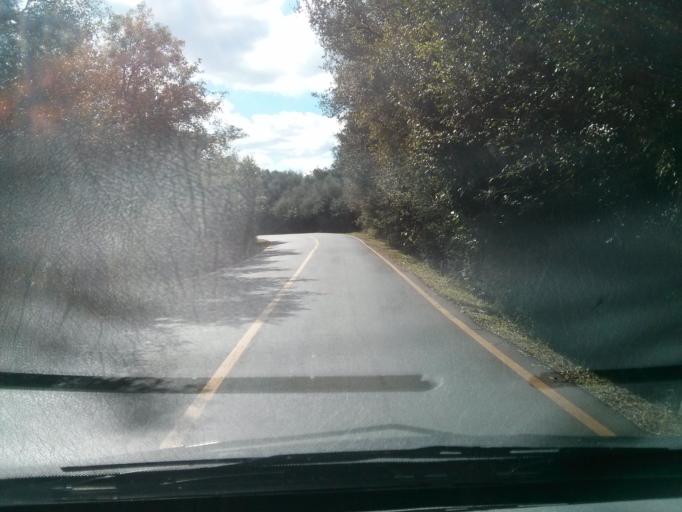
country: BR
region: Parana
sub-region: Sao Jose Dos Pinhais
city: Sao Jose dos Pinhais
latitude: -25.5483
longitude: -49.2237
